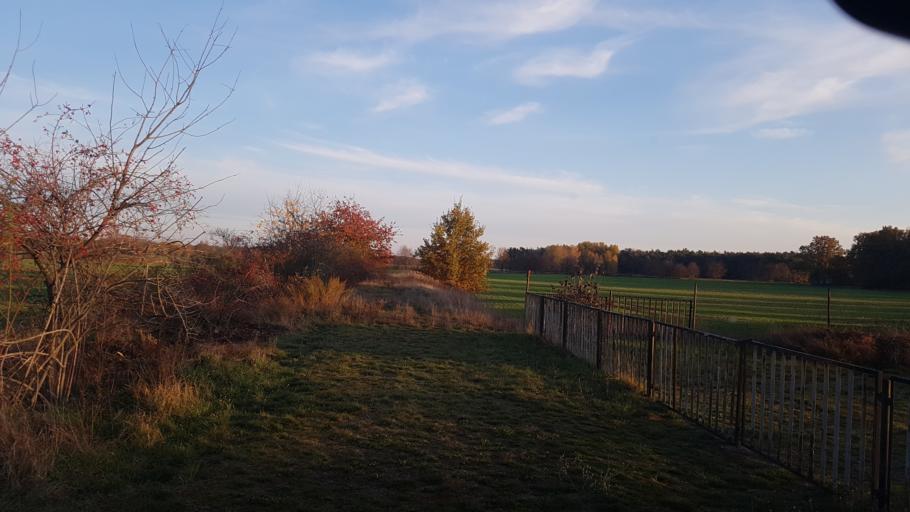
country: DE
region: Brandenburg
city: Falkenberg
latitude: 51.5961
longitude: 13.3117
